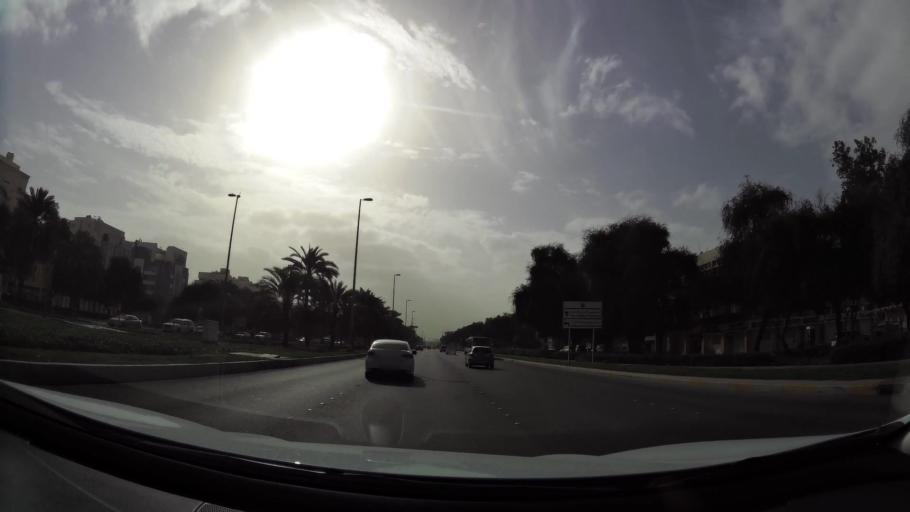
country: AE
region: Abu Dhabi
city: Abu Dhabi
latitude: 24.4482
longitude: 54.3996
